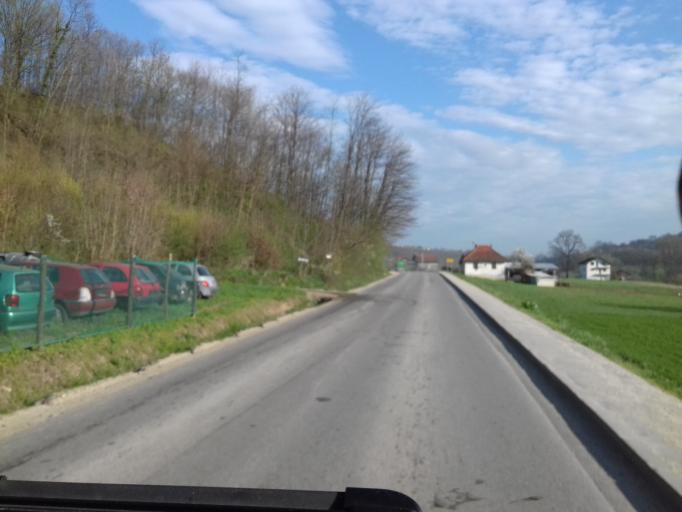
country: BA
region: Federation of Bosnia and Herzegovina
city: Tesanjka
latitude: 44.6451
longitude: 18.0191
